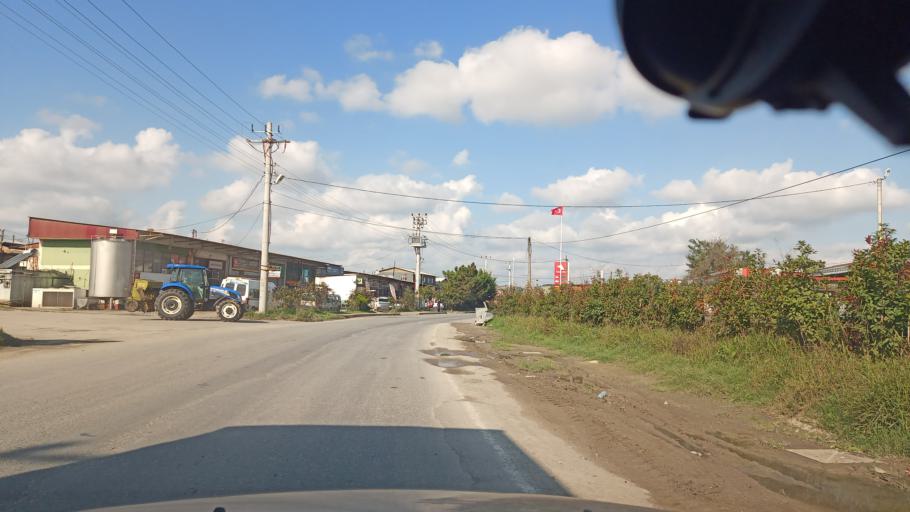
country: TR
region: Sakarya
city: Kaynarca
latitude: 41.0262
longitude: 30.3086
